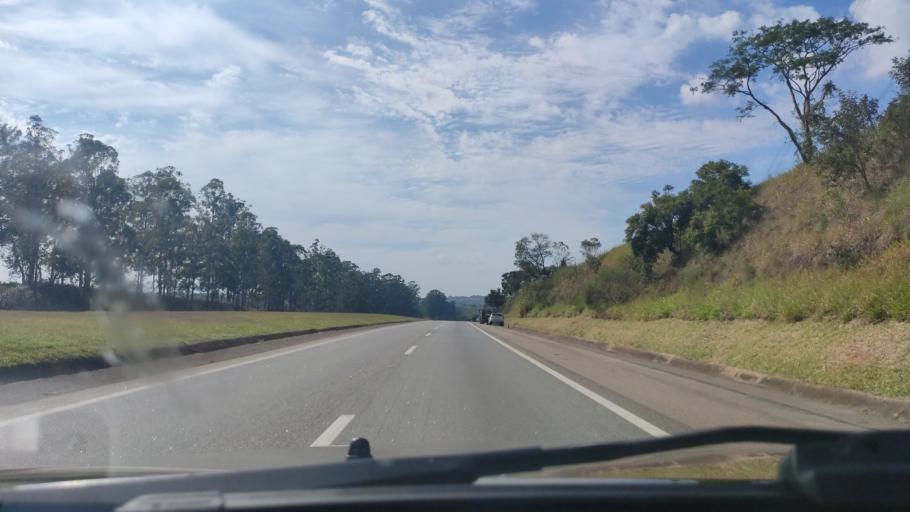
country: BR
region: Sao Paulo
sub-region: Tatui
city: Tatui
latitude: -23.2840
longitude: -47.7818
